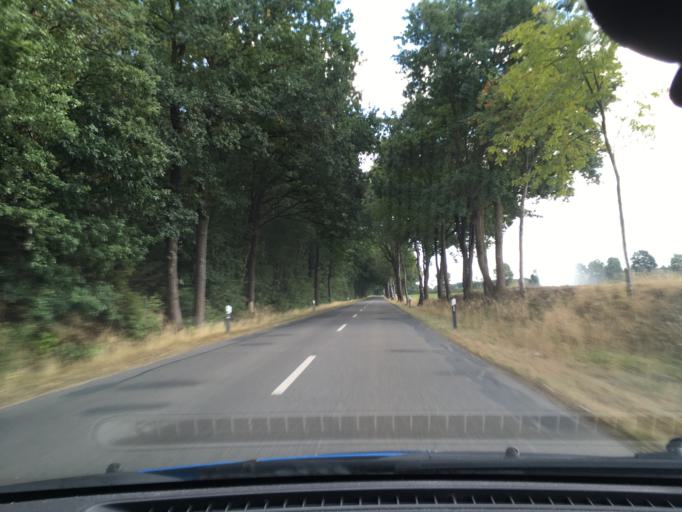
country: DE
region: Lower Saxony
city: Wriedel
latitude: 53.0442
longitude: 10.2641
